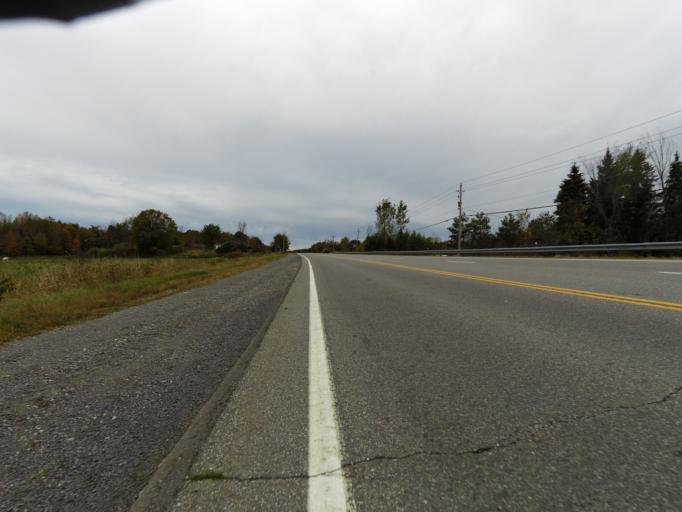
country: CA
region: Ontario
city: Gananoque
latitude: 44.4332
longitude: -76.2887
